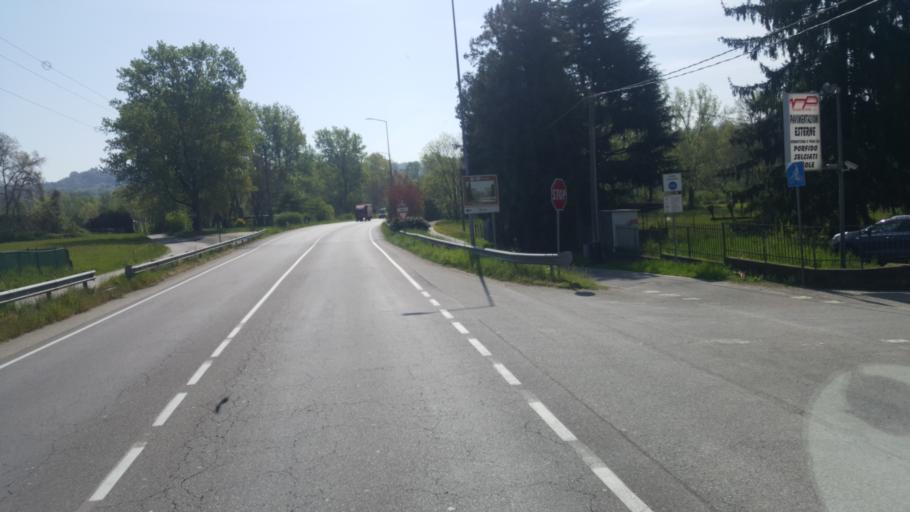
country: IT
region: Lombardy
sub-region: Provincia di Varese
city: Buguggiate
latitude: 45.8045
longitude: 8.7992
